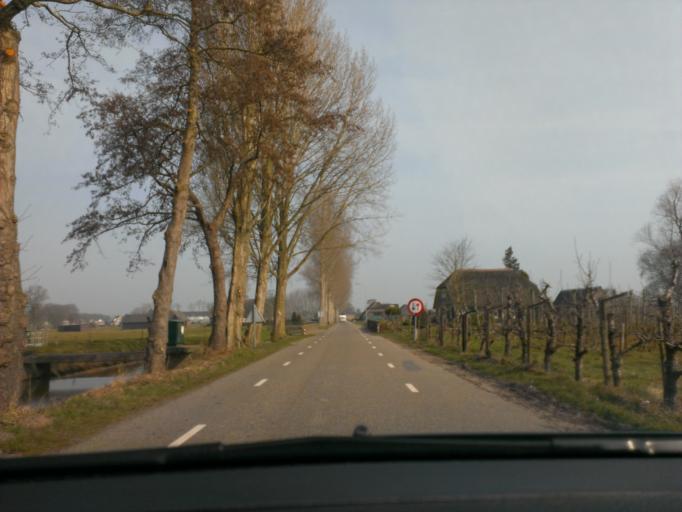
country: NL
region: Gelderland
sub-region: Gemeente Voorst
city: Twello
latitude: 52.2525
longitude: 6.0375
